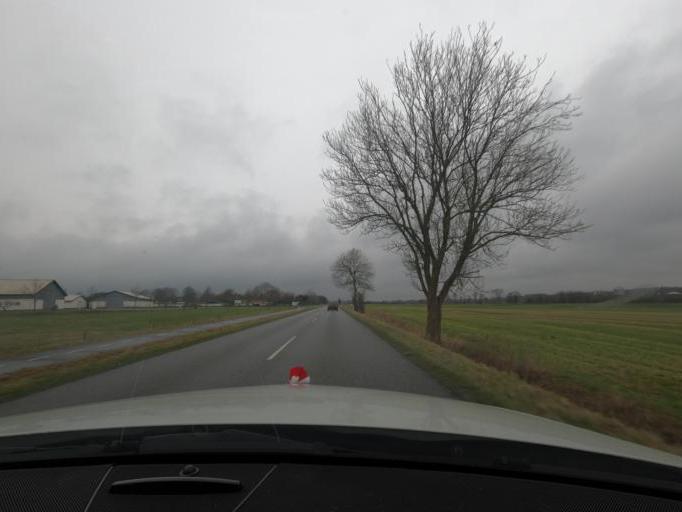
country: DK
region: South Denmark
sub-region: Haderslev Kommune
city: Starup
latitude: 55.2067
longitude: 9.5199
